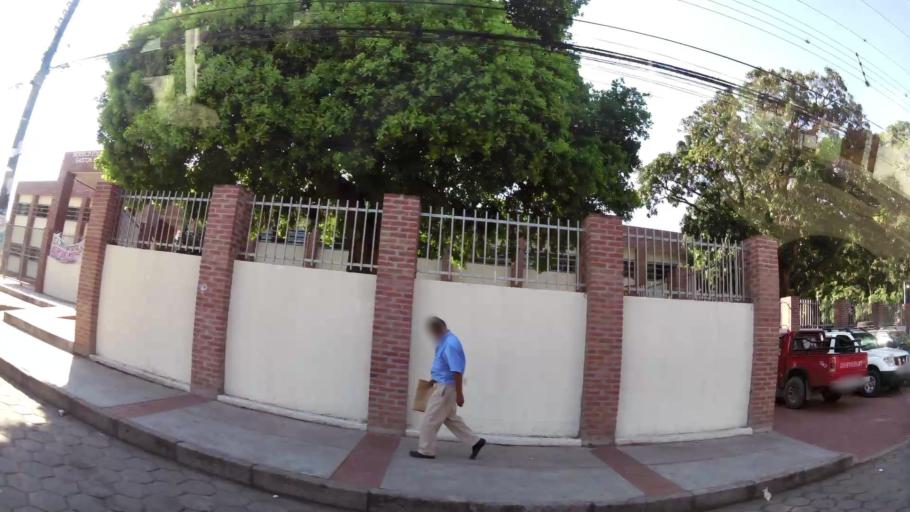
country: BO
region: Santa Cruz
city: Santa Cruz de la Sierra
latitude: -17.7792
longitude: -63.1710
